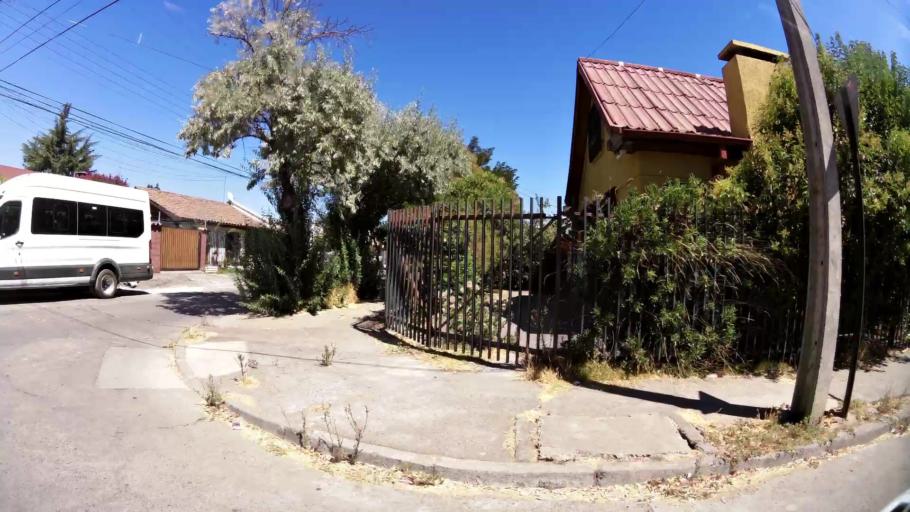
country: CL
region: O'Higgins
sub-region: Provincia de Cachapoal
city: Rancagua
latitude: -34.1629
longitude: -70.7478
